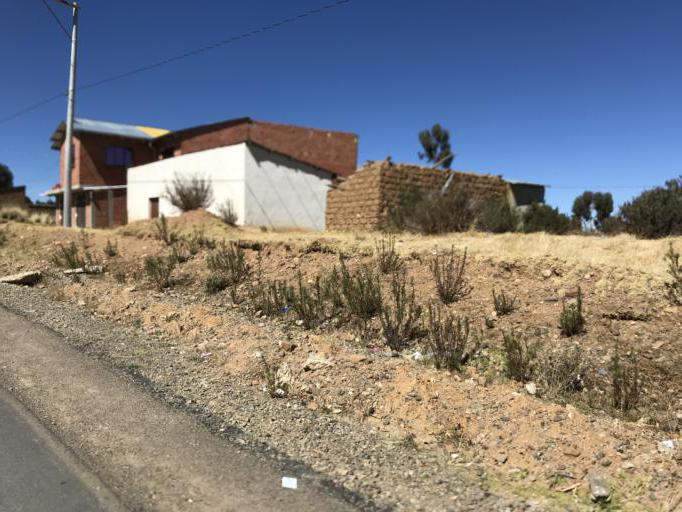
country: BO
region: La Paz
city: Huatajata
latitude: -16.2142
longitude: -68.6595
